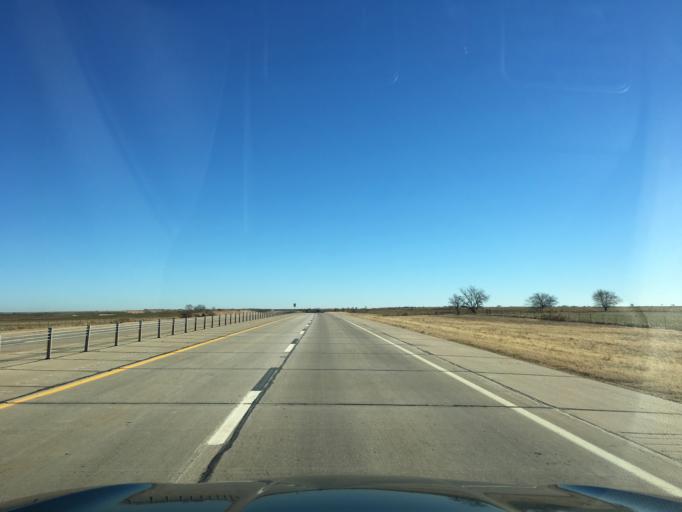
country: US
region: Oklahoma
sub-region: Noble County
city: Perry
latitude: 36.3997
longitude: -97.2414
